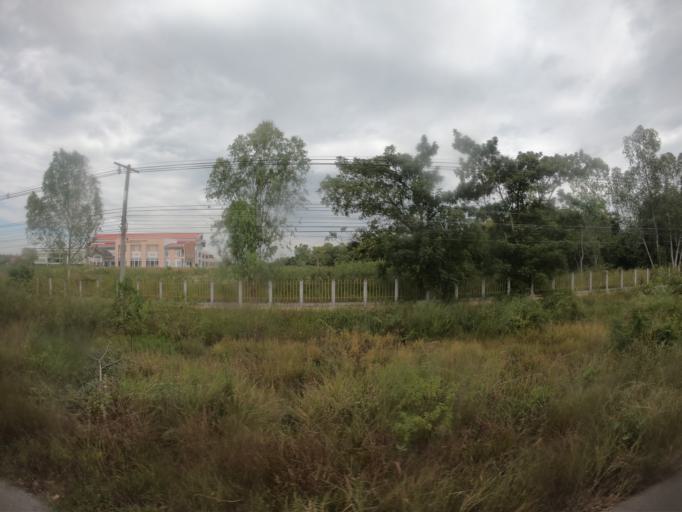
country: TH
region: Maha Sarakham
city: Kantharawichai
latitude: 16.3394
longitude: 103.2083
